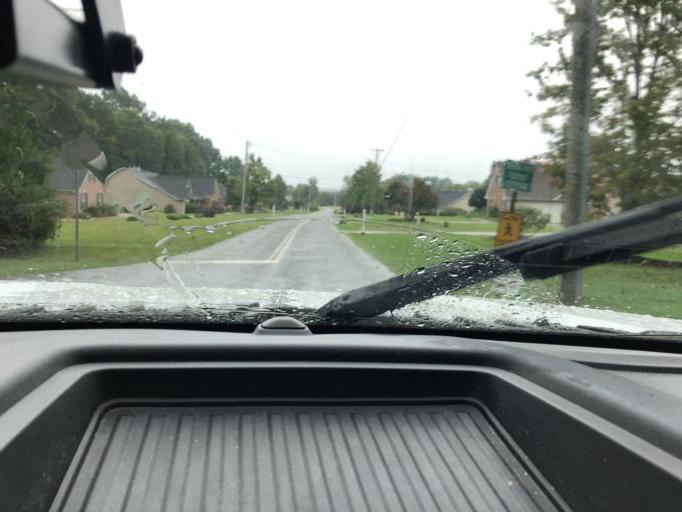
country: US
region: Georgia
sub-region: Putnam County
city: Jefferson
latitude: 33.3911
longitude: -83.2494
